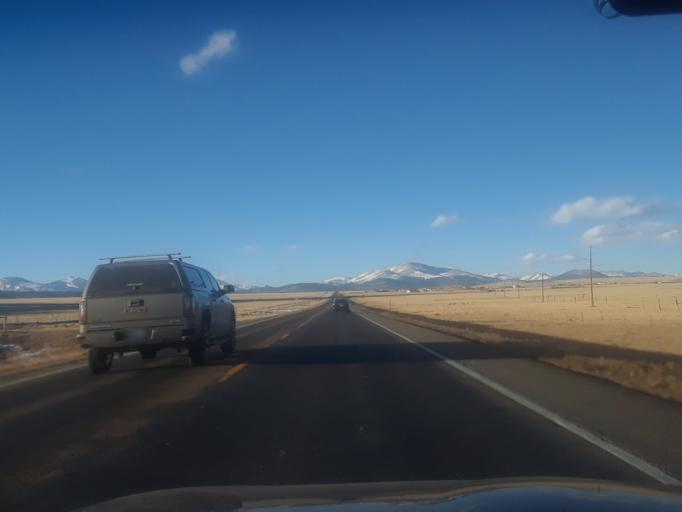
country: US
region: Colorado
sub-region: Park County
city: Fairplay
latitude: 39.1046
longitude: -105.9901
